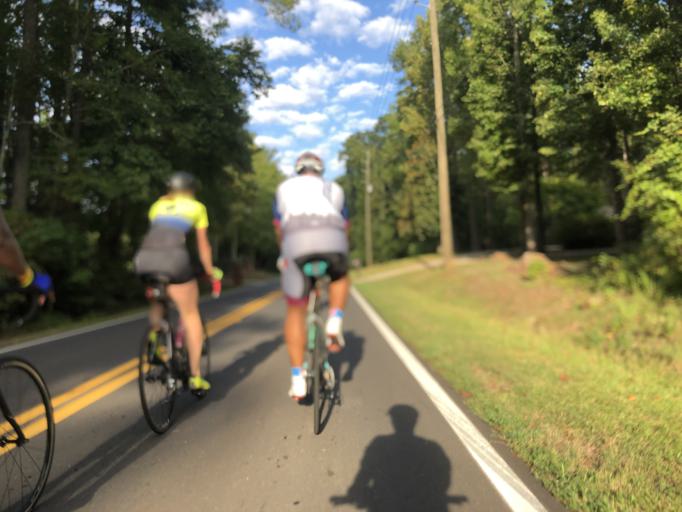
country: US
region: Georgia
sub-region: Fulton County
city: Palmetto
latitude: 33.5741
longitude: -84.6577
